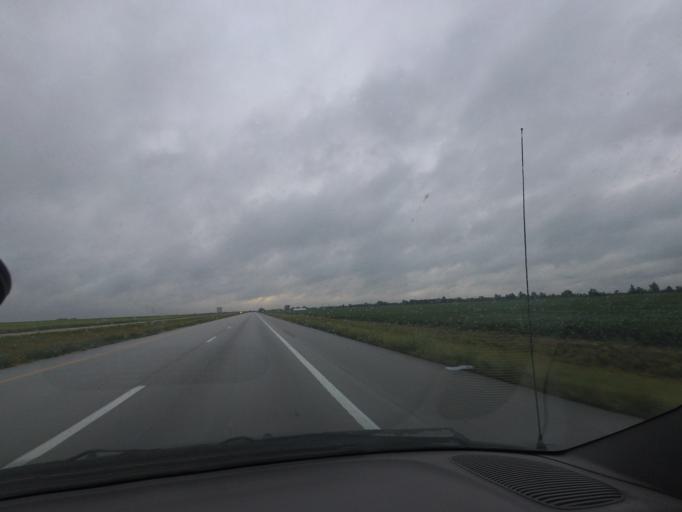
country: US
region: Missouri
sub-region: Marion County
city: Monroe City
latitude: 39.6646
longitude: -91.6961
